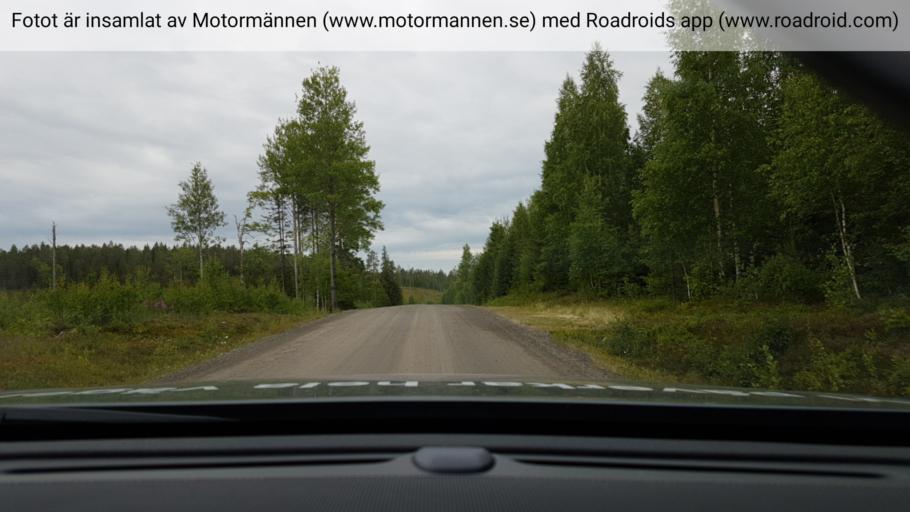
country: SE
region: Vaesterbotten
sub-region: Umea Kommun
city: Ersmark
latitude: 64.1220
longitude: 20.1360
